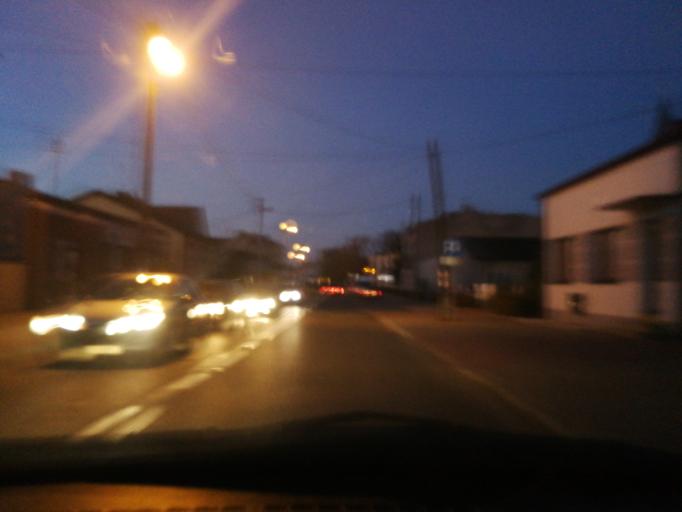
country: PL
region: Lodz Voivodeship
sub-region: Powiat brzezinski
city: Jezow
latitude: 51.8136
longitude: 19.9690
